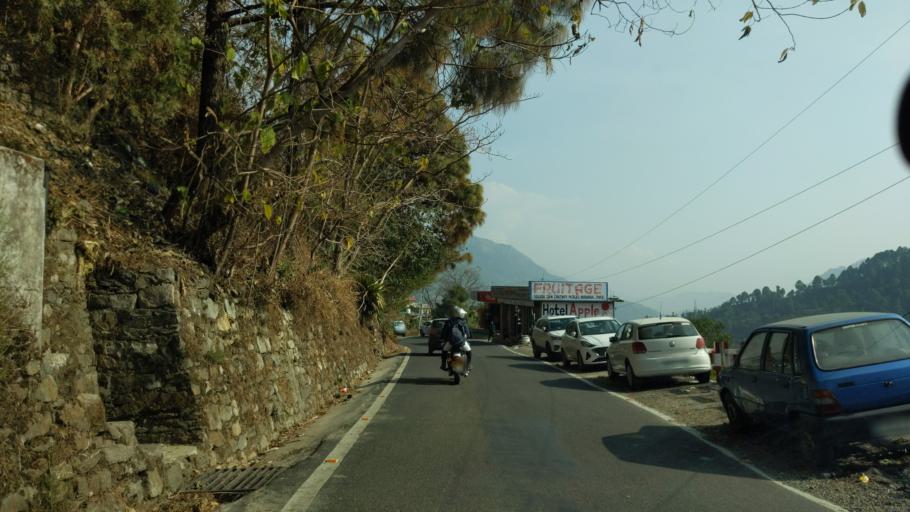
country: IN
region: Uttarakhand
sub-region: Naini Tal
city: Bhowali
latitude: 29.3791
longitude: 79.5247
